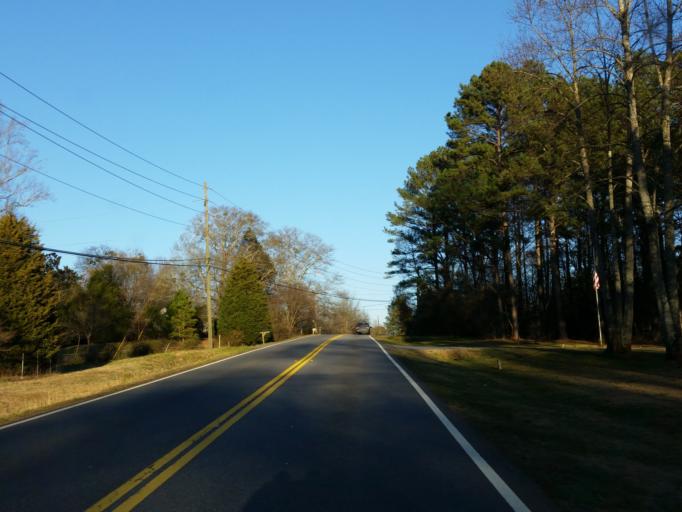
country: US
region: Georgia
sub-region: Cherokee County
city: Holly Springs
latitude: 34.1388
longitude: -84.4653
